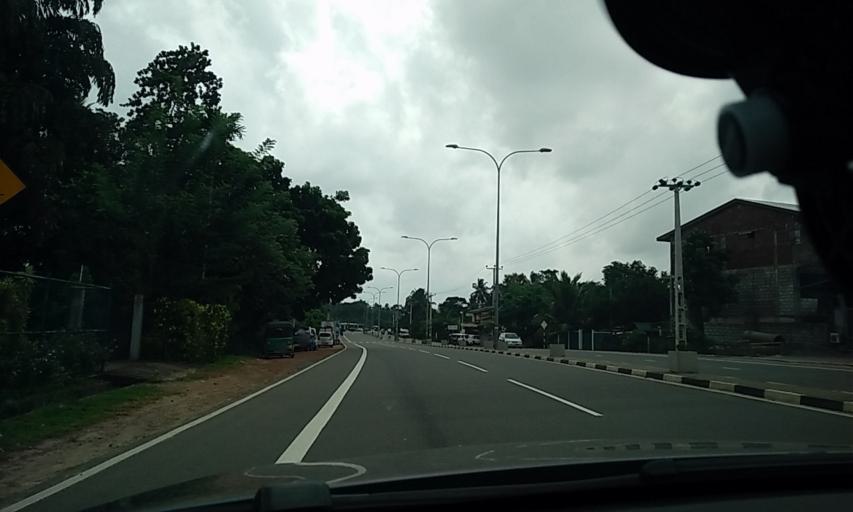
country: LK
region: Western
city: Maharagama
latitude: 6.8019
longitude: 79.9334
